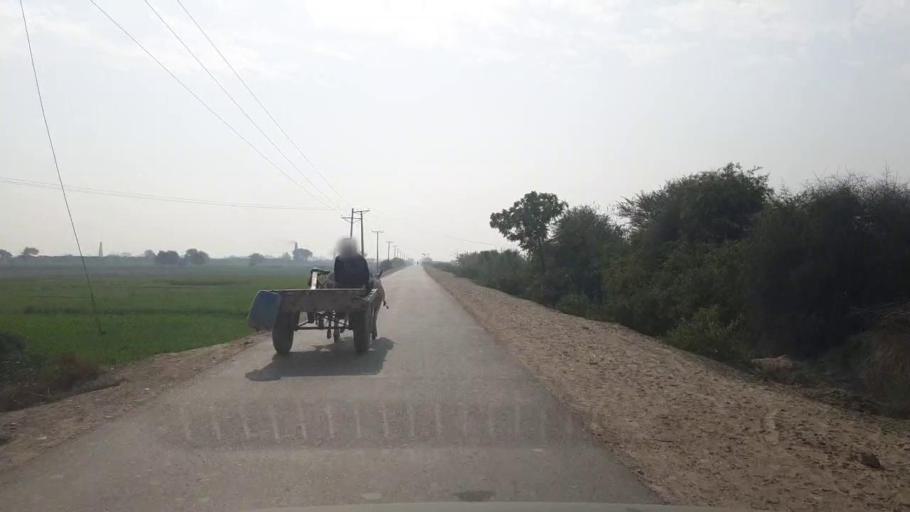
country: PK
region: Sindh
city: Hala
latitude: 25.7802
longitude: 68.4433
